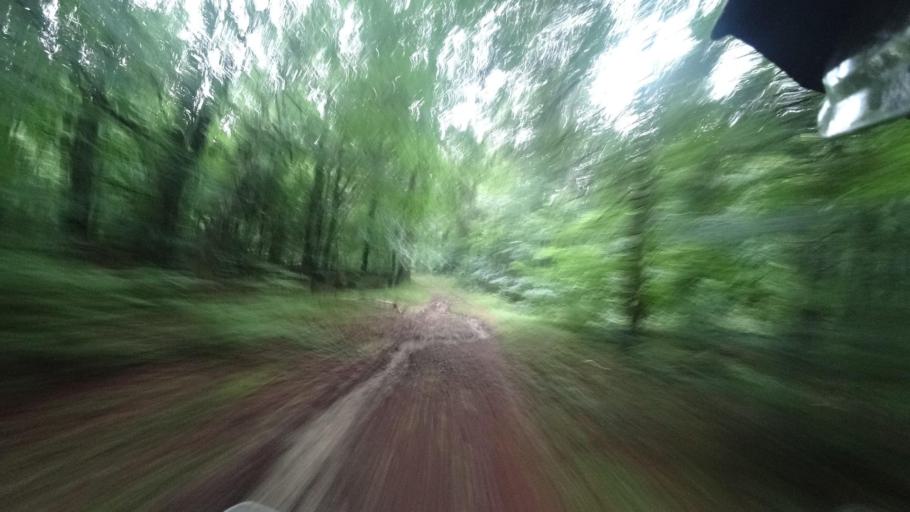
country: HR
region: Licko-Senjska
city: Jezerce
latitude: 44.8208
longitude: 15.6177
